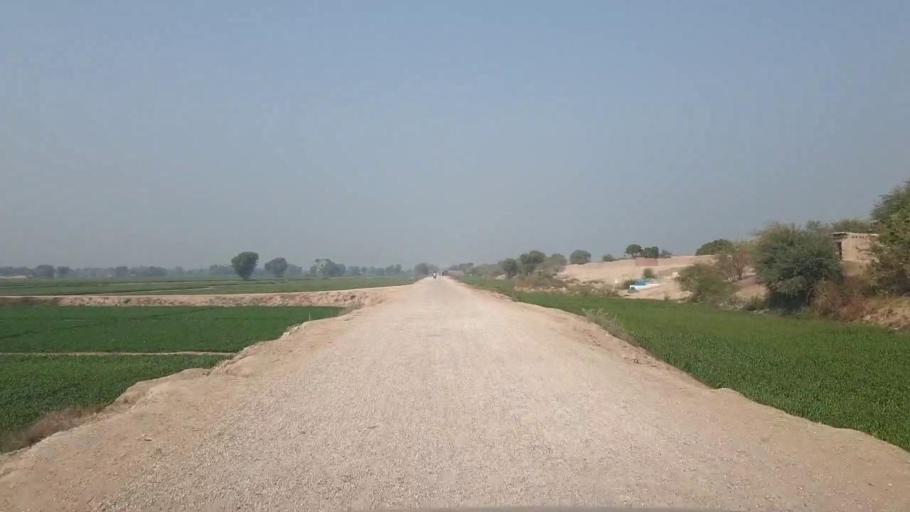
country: PK
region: Sindh
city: Hala
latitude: 25.8147
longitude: 68.4113
